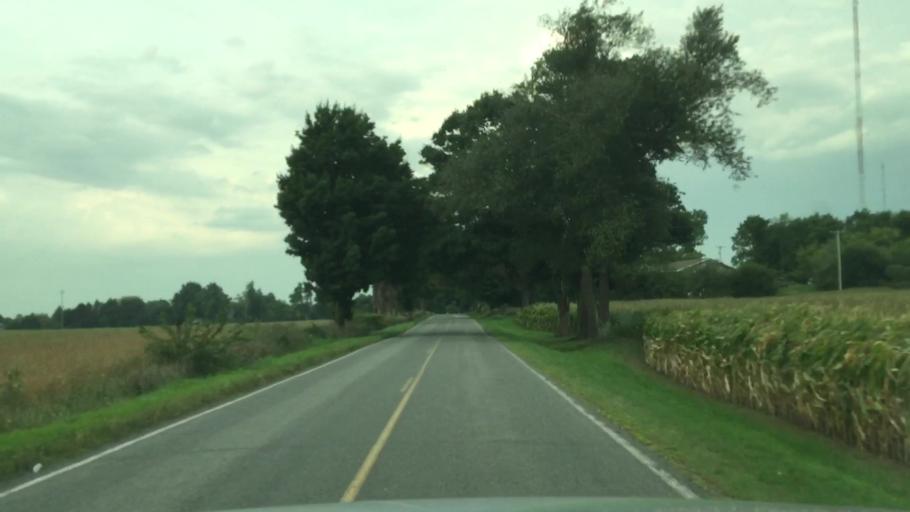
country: US
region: Michigan
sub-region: Shiawassee County
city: Perry
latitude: 42.8965
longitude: -84.1771
